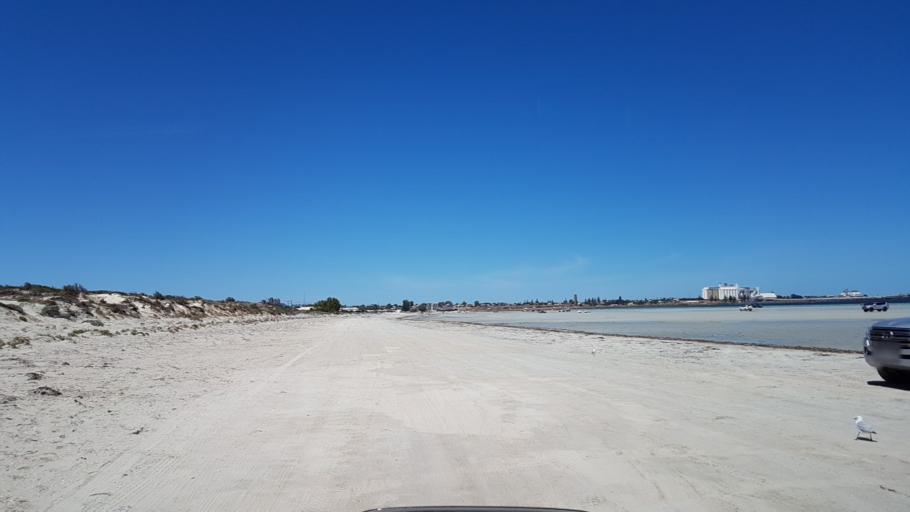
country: AU
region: South Australia
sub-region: Copper Coast
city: Wallaroo
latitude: -33.9078
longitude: 137.6309
